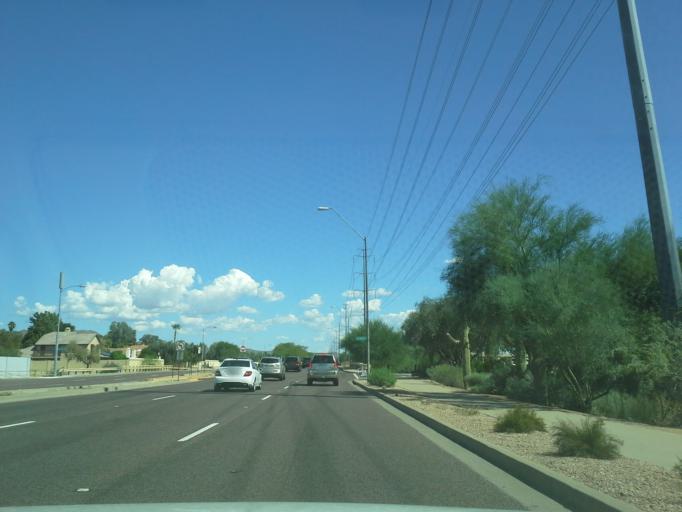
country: US
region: Arizona
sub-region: Maricopa County
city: Scottsdale
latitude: 33.5824
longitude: -111.8661
